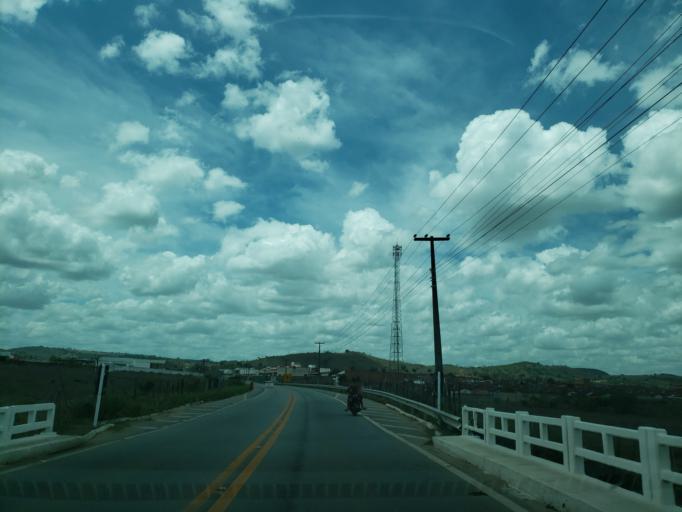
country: BR
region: Alagoas
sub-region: Uniao Dos Palmares
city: Uniao dos Palmares
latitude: -9.1545
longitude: -36.0130
